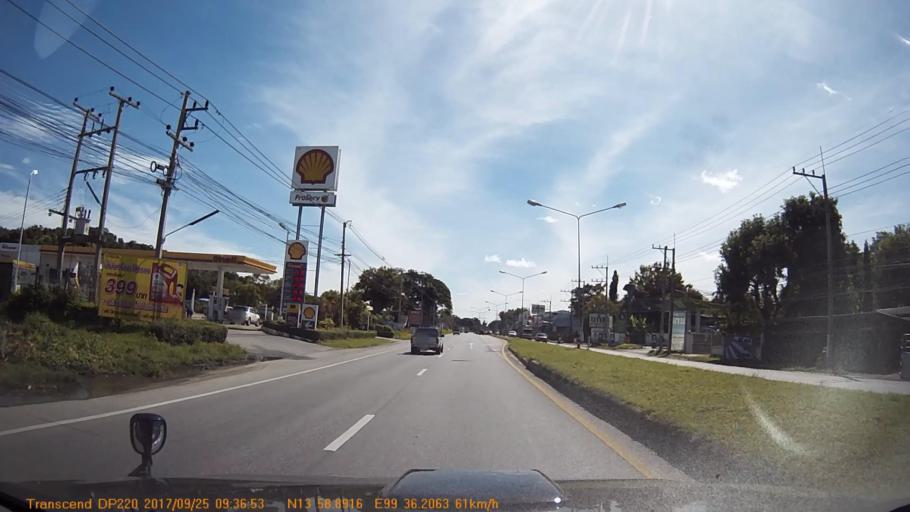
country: TH
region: Kanchanaburi
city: Tha Muang
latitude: 13.9816
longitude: 99.6037
